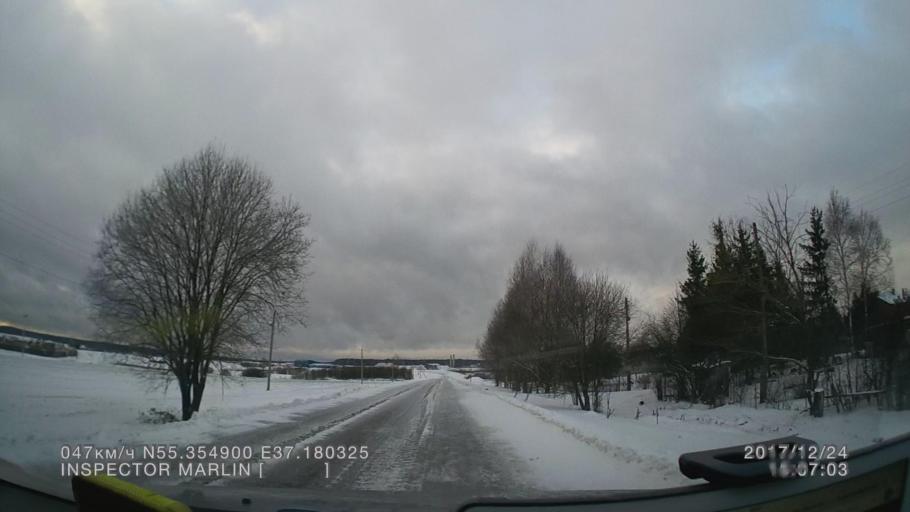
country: RU
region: Moskovskaya
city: Troitsk
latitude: 55.3549
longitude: 37.1803
